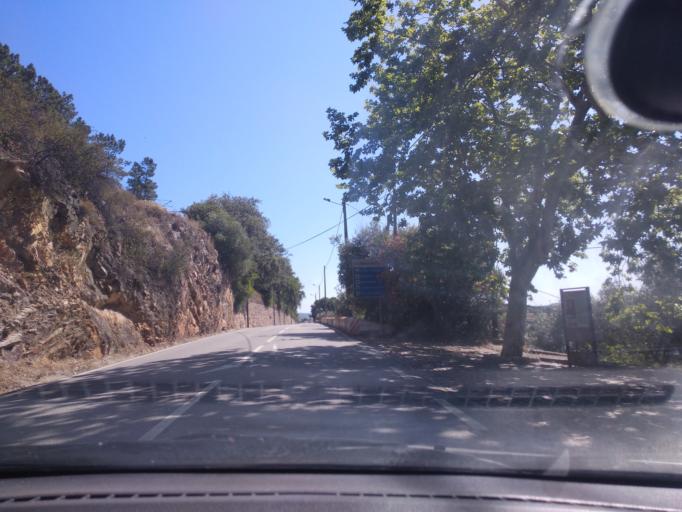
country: PT
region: Portalegre
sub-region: Nisa
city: Nisa
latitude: 39.6483
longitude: -7.6764
